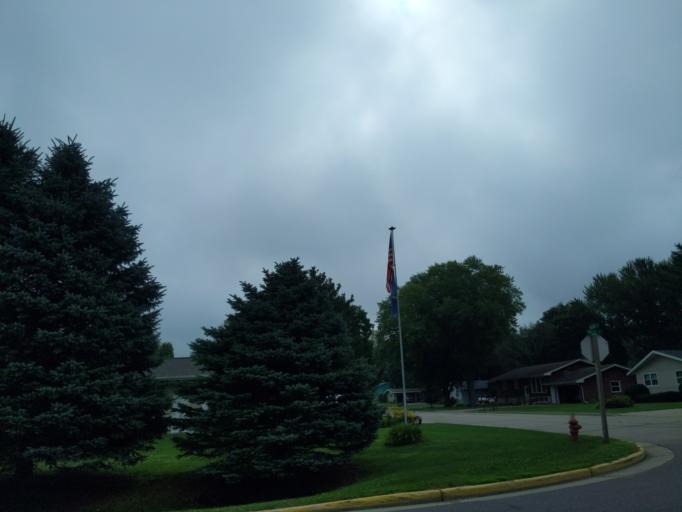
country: US
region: Wisconsin
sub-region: Dane County
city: Black Earth
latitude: 43.1304
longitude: -89.7481
